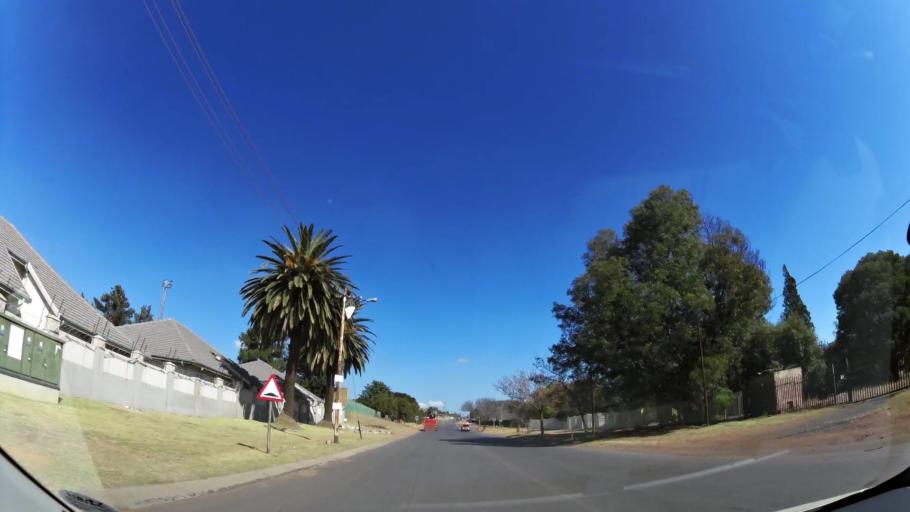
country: ZA
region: Mpumalanga
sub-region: Nkangala District Municipality
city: Witbank
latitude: -25.8525
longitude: 29.2467
